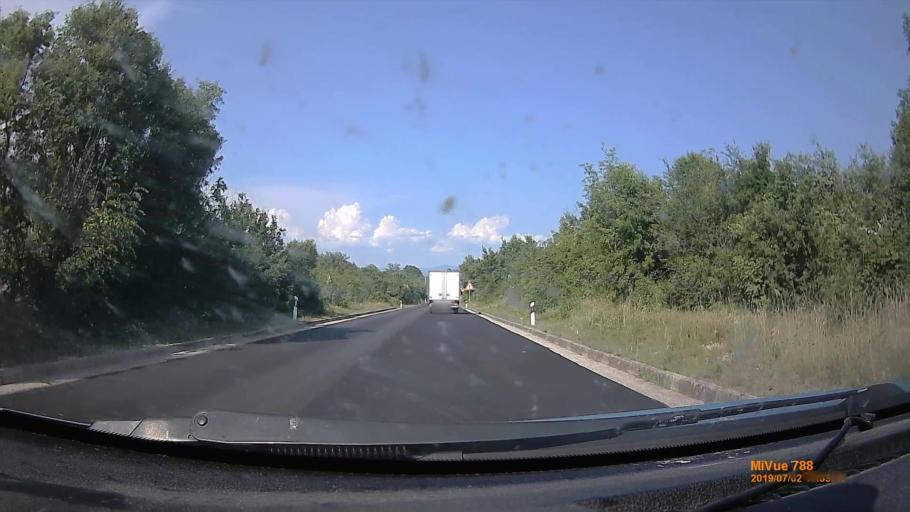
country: HR
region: Primorsko-Goranska
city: Njivice
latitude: 45.0755
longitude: 14.4925
